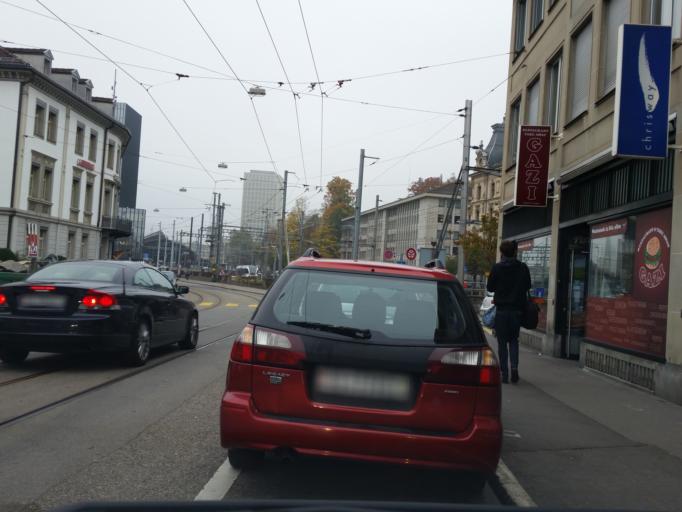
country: CH
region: Saint Gallen
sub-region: Wahlkreis St. Gallen
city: Sankt Gallen
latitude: 47.4257
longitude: 9.3730
